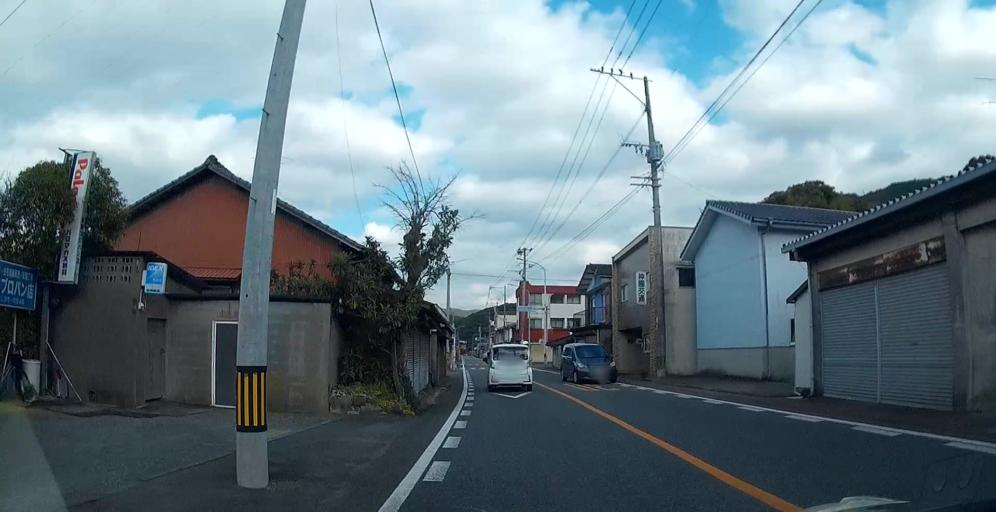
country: JP
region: Kumamoto
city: Yatsushiro
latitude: 32.4361
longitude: 130.5808
